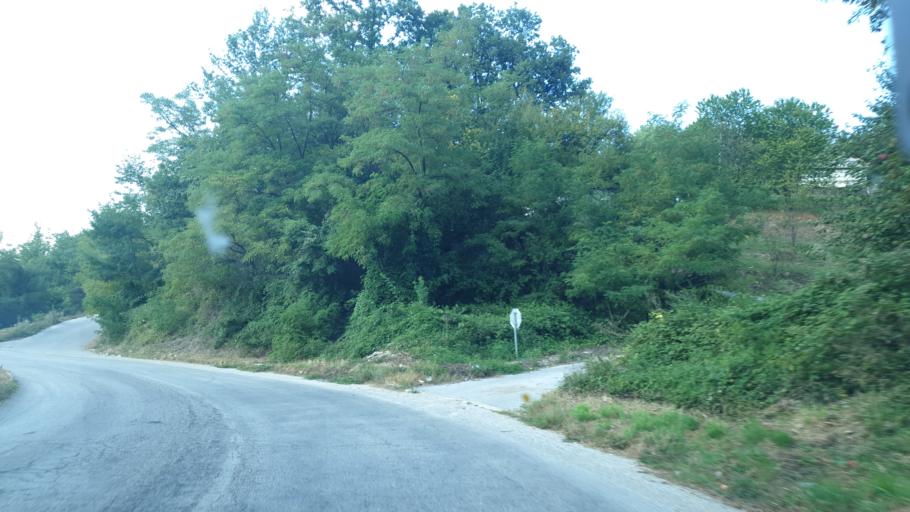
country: RS
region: Central Serbia
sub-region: Zlatiborski Okrug
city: Uzice
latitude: 43.8623
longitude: 19.9082
